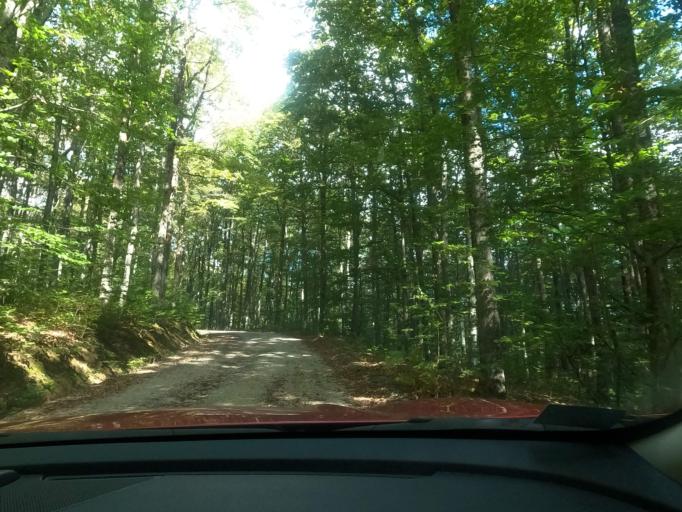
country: BA
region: Federation of Bosnia and Herzegovina
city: Velika Kladusa
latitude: 45.2486
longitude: 15.7706
